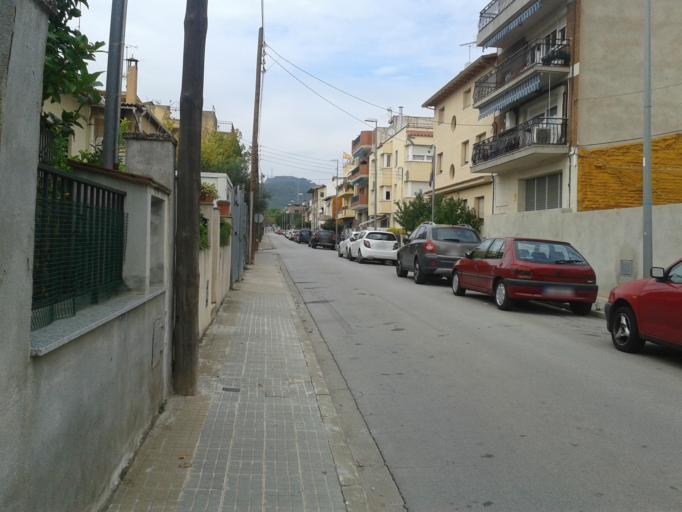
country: ES
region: Catalonia
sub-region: Provincia de Barcelona
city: Sentmenat
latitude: 41.6112
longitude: 2.1331
